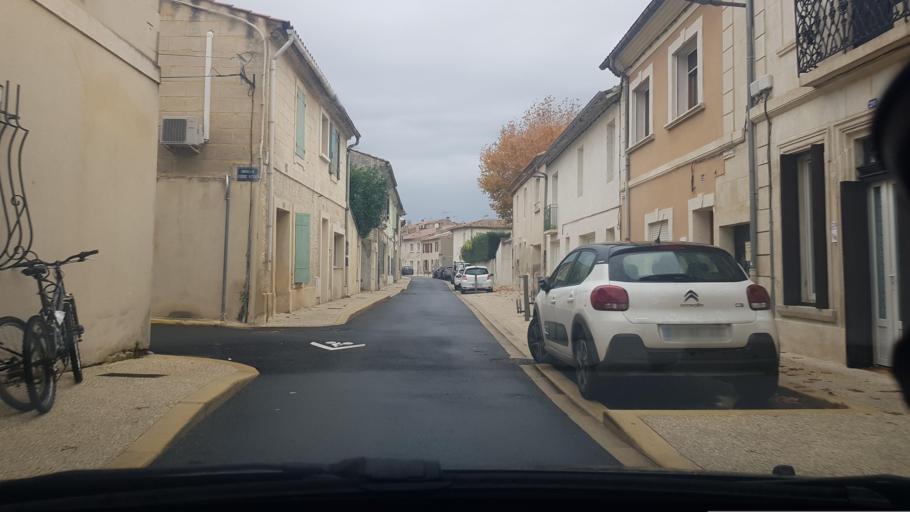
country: FR
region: Languedoc-Roussillon
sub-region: Departement du Gard
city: Bellegarde
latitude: 43.7547
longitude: 4.5129
